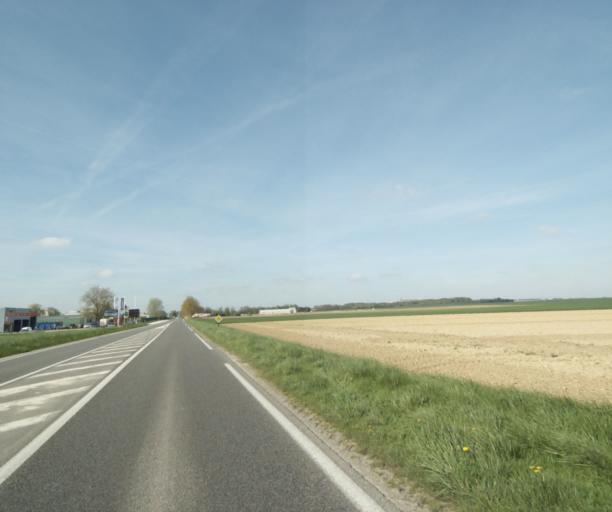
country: FR
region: Ile-de-France
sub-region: Departement de Seine-et-Marne
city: Nangis
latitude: 48.5638
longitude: 3.0377
